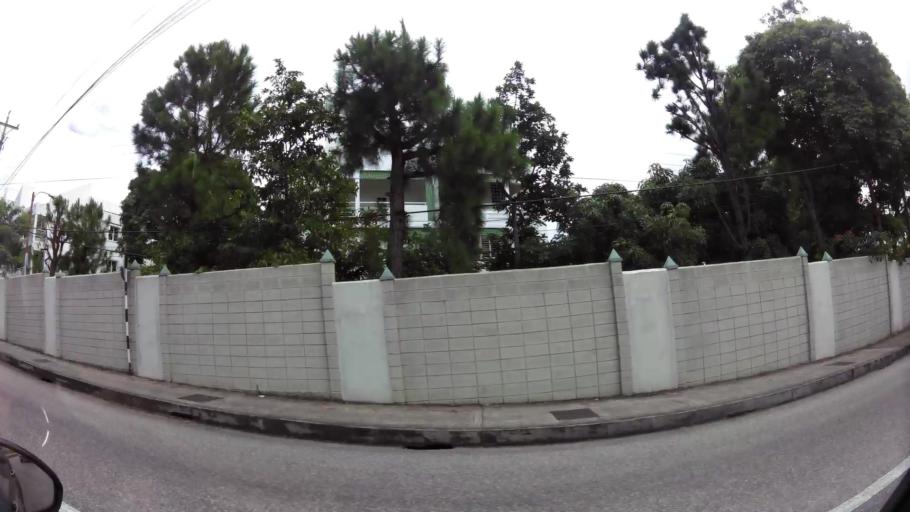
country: TT
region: City of Port of Spain
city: Port-of-Spain
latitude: 10.6776
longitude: -61.5304
